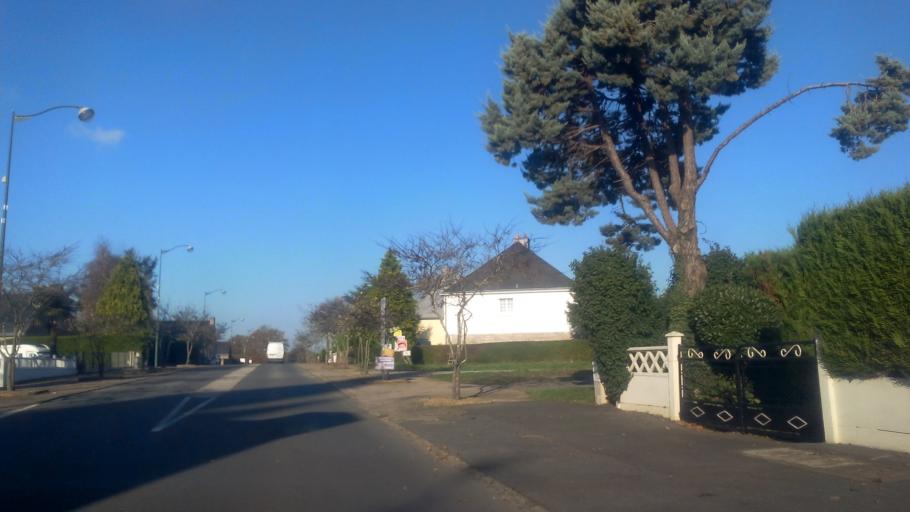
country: FR
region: Brittany
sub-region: Departement du Morbihan
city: Saint-Vincent-sur-Oust
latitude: 47.7007
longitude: -2.1477
